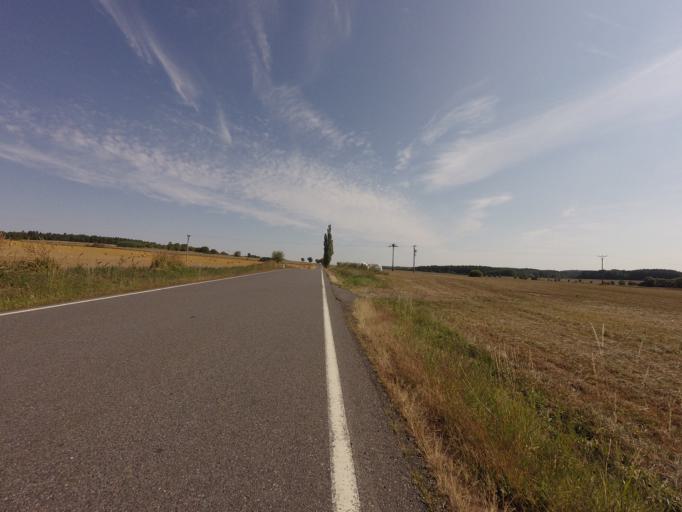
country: CZ
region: Jihocesky
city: Bernartice
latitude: 49.3461
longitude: 14.3699
